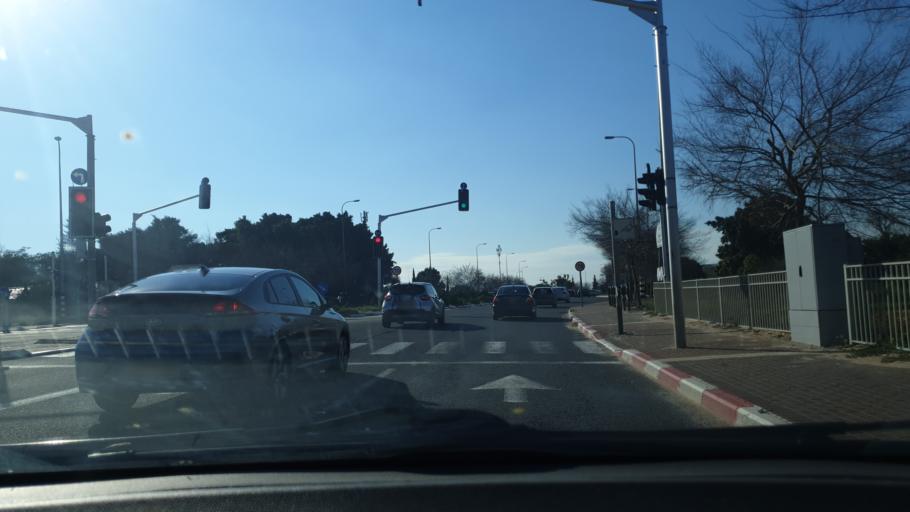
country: IL
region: Central District
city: Ness Ziona
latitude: 31.9438
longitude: 34.8259
